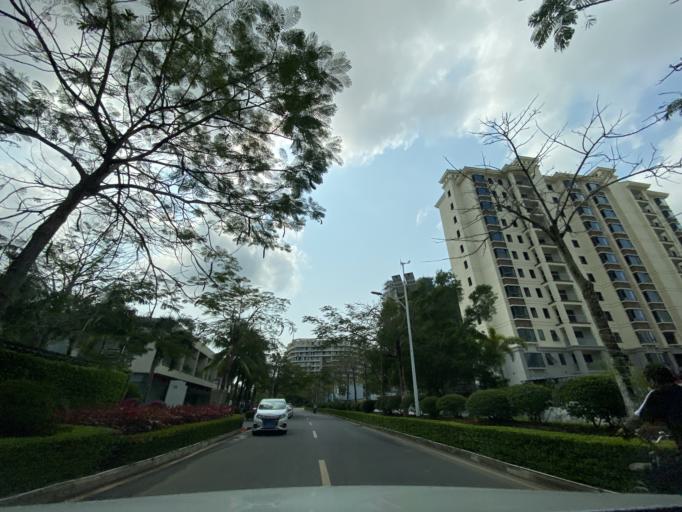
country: CN
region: Hainan
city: Yingzhou
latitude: 18.4115
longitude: 109.8520
